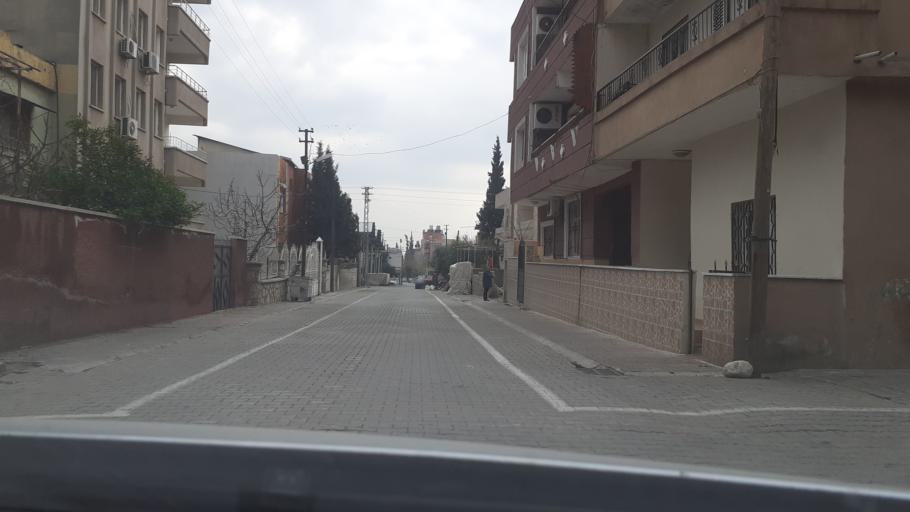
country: TR
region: Hatay
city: Kirikhan
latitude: 36.4937
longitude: 36.3523
